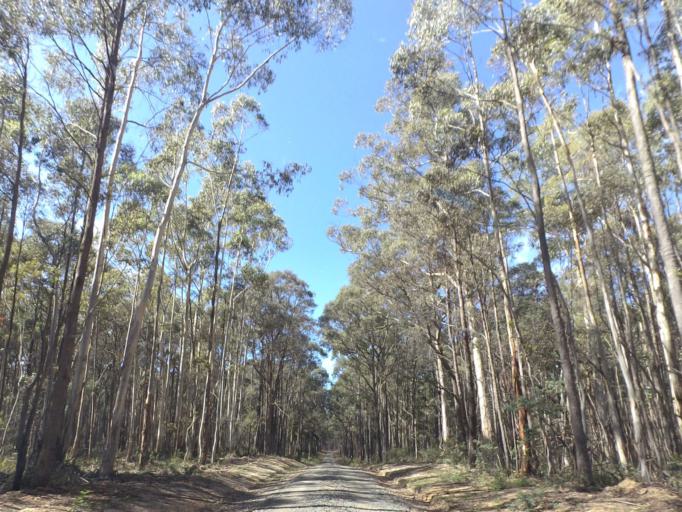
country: AU
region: Victoria
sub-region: Moorabool
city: Bacchus Marsh
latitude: -37.4136
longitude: 144.3328
